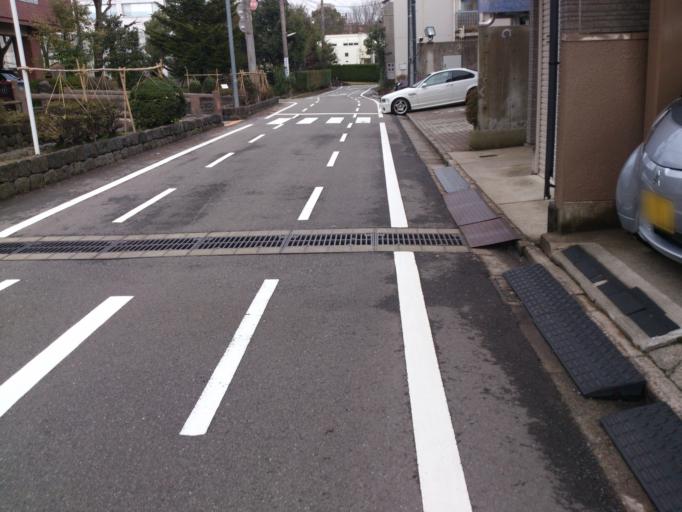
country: JP
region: Ishikawa
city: Kanazawa-shi
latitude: 36.5672
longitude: 136.6512
